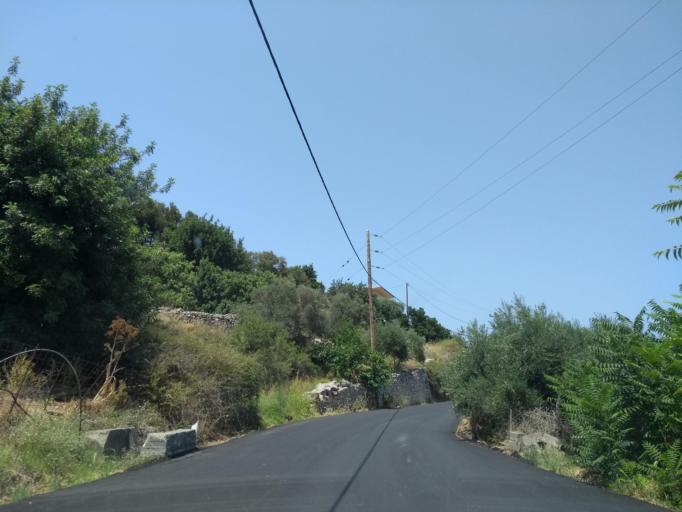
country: GR
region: Crete
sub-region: Nomos Chanias
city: Georgioupolis
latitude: 35.3193
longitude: 24.2994
